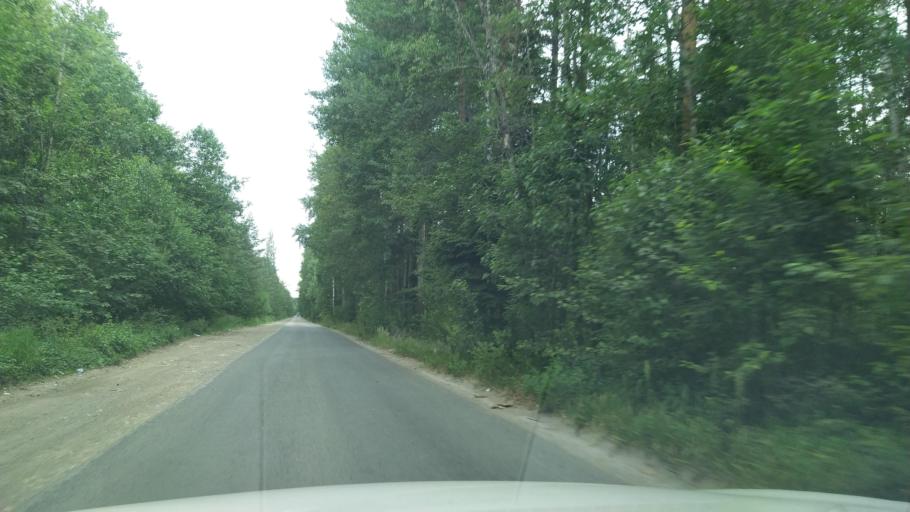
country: RU
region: St.-Petersburg
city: Bol'shaya Izhora
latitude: 59.9164
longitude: 29.5717
